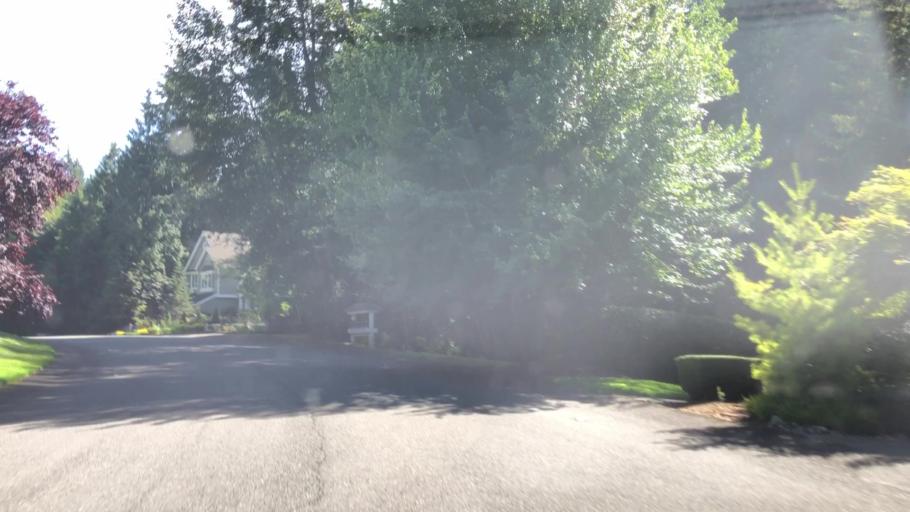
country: US
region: Washington
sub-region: King County
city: Cottage Lake
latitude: 47.7087
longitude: -122.0749
